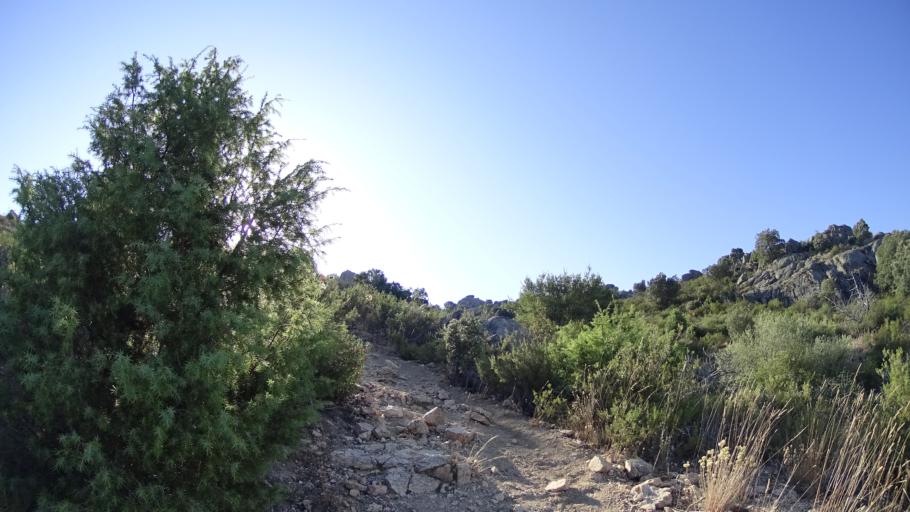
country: ES
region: Madrid
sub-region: Provincia de Madrid
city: Moralzarzal
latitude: 40.6486
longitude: -3.9559
